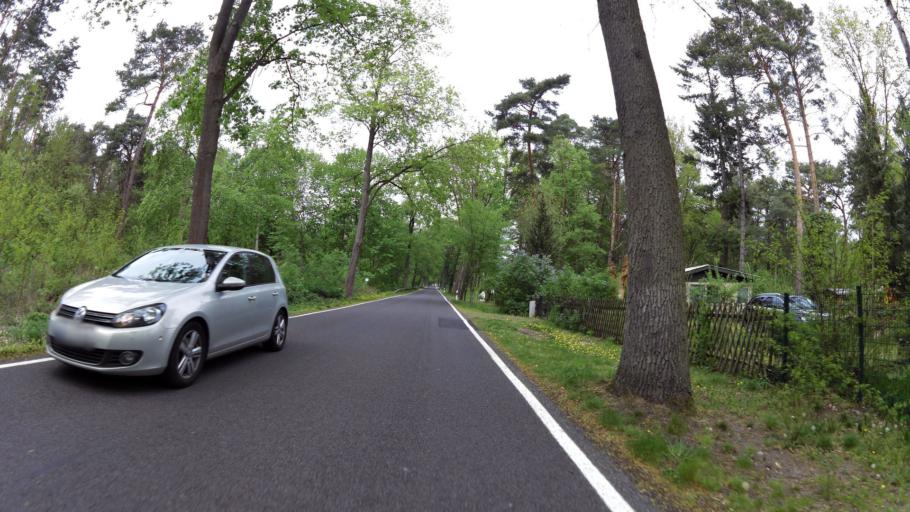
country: DE
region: Brandenburg
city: Mittenwalde
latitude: 52.1973
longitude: 13.5767
